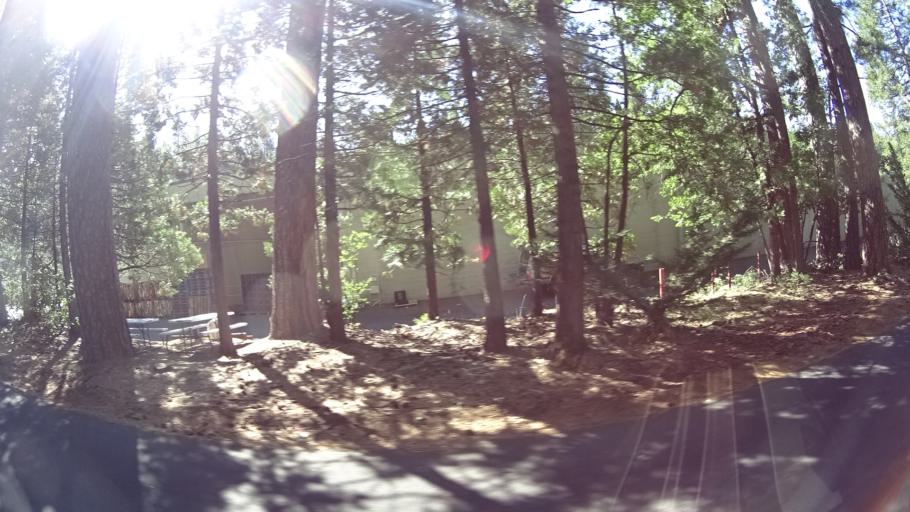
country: US
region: California
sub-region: Calaveras County
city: Arnold
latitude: 38.2401
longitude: -120.3642
